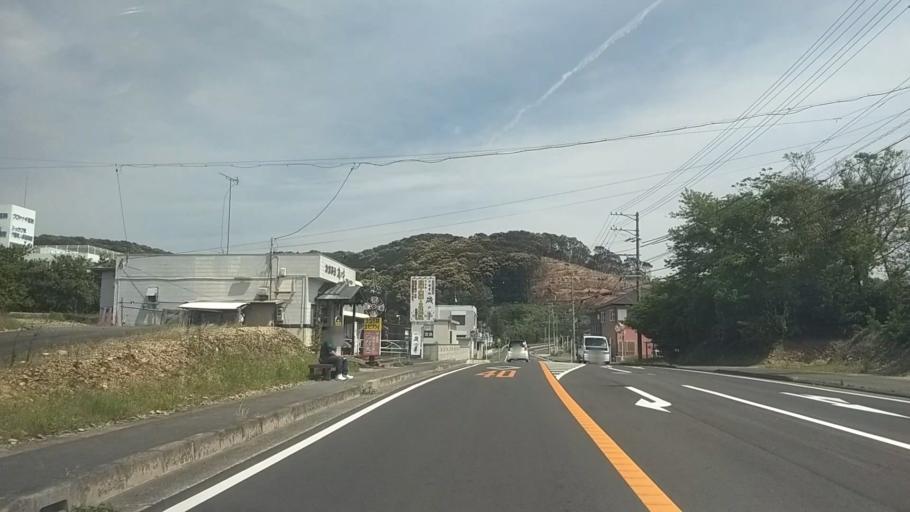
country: JP
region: Shizuoka
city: Kosai-shi
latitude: 34.8004
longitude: 137.5593
